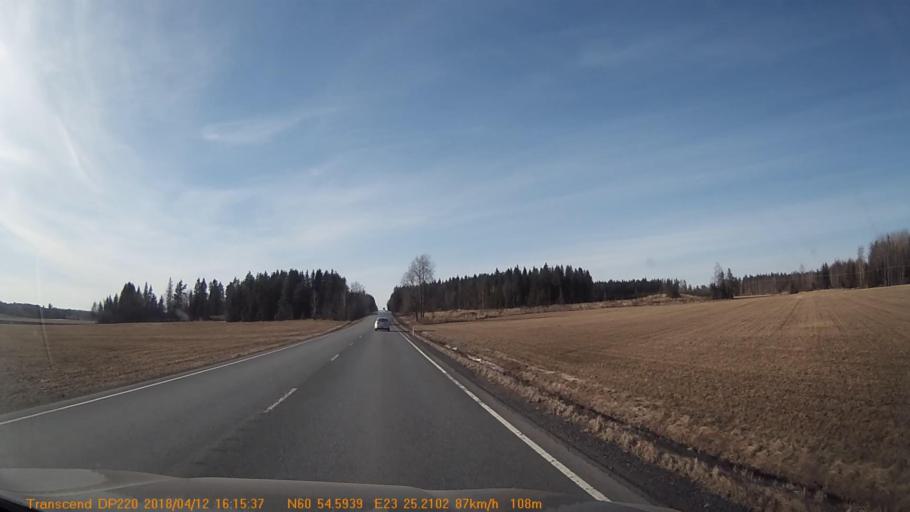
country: FI
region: Haeme
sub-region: Forssa
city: Humppila
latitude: 60.9100
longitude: 23.4199
